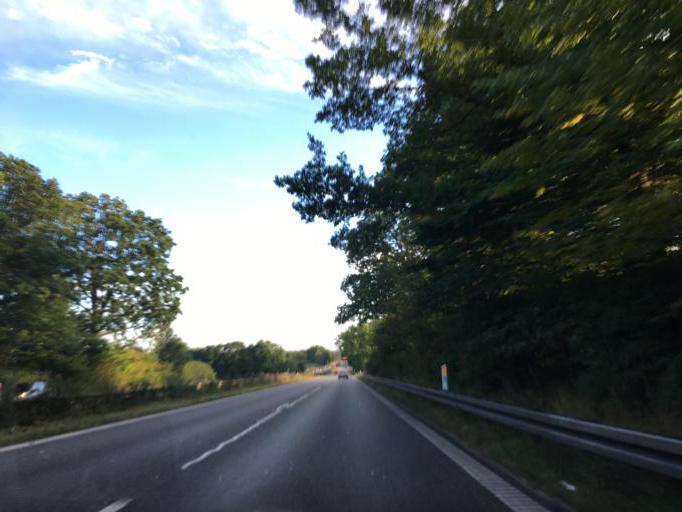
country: DK
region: Capital Region
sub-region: Horsholm Kommune
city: Horsholm
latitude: 55.8927
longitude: 12.4761
